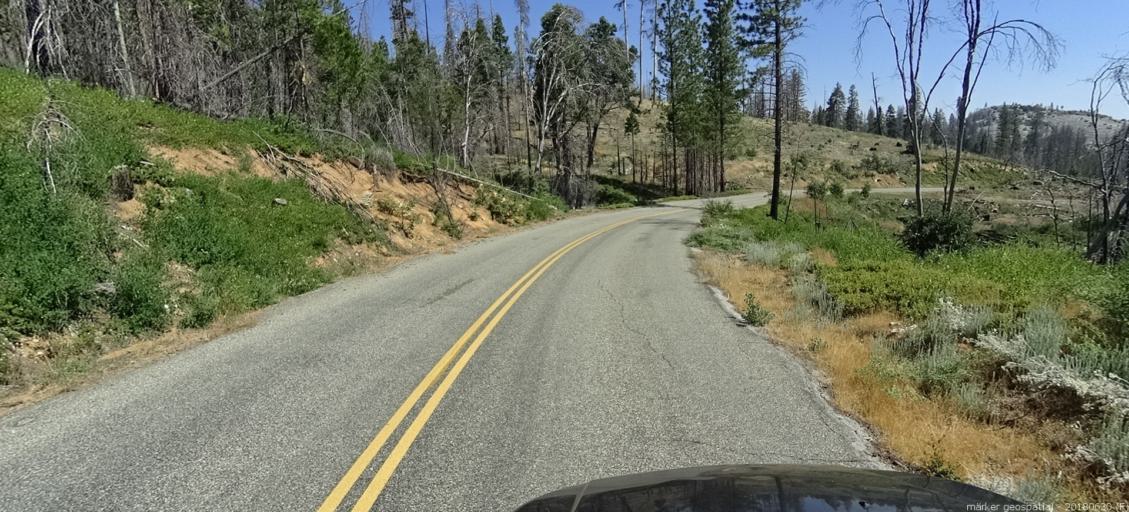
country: US
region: California
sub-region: Fresno County
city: Auberry
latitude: 37.3293
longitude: -119.3685
